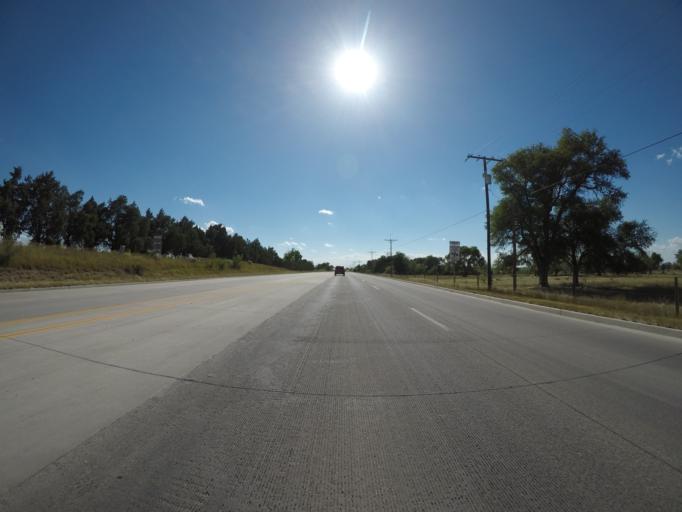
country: US
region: Colorado
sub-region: Logan County
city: Sterling
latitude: 40.6241
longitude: -103.2522
